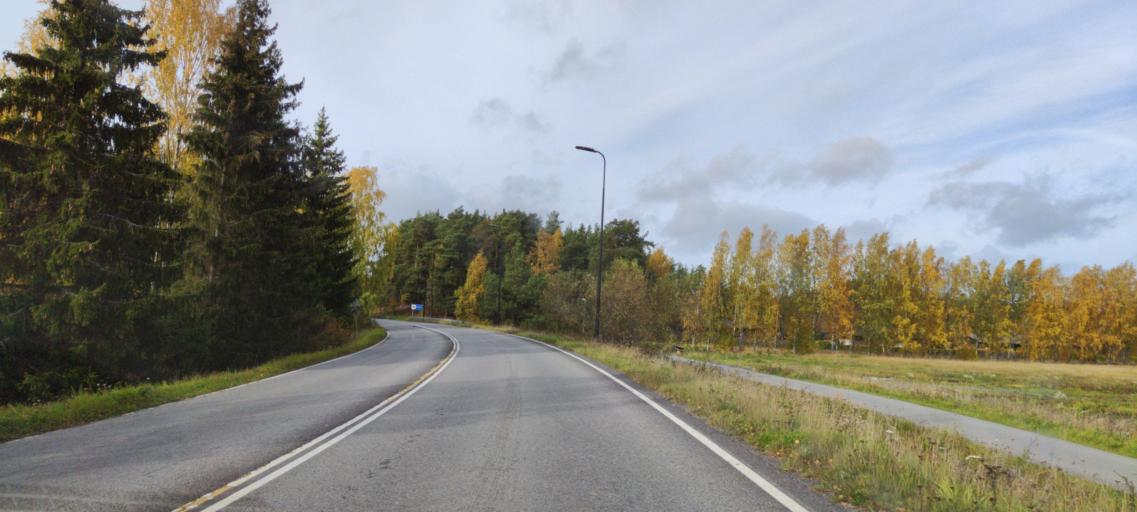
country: FI
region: Varsinais-Suomi
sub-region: Turku
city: Raisio
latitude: 60.4755
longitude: 22.2045
